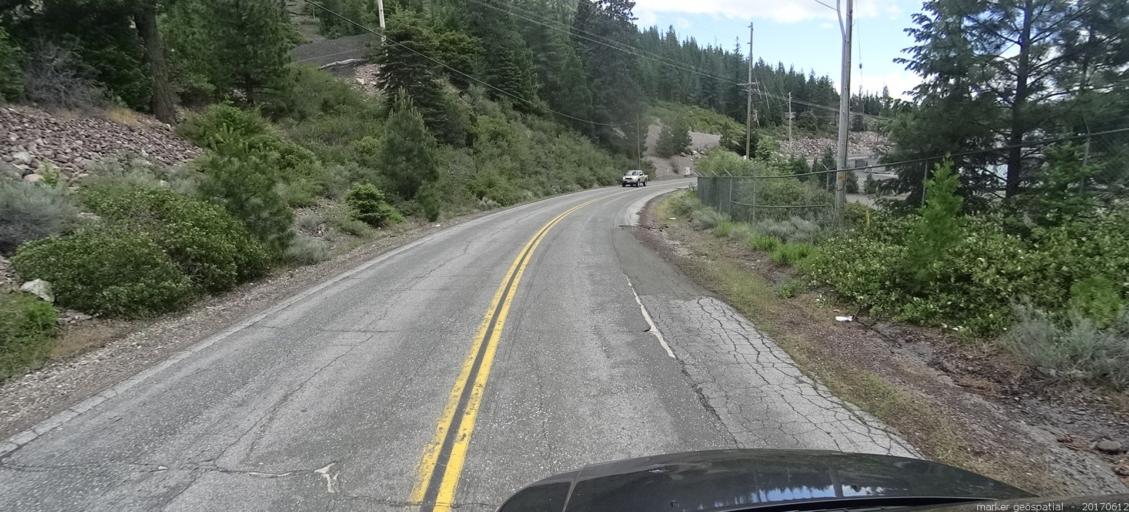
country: US
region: California
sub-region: Siskiyou County
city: Weed
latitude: 41.3699
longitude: -122.3684
